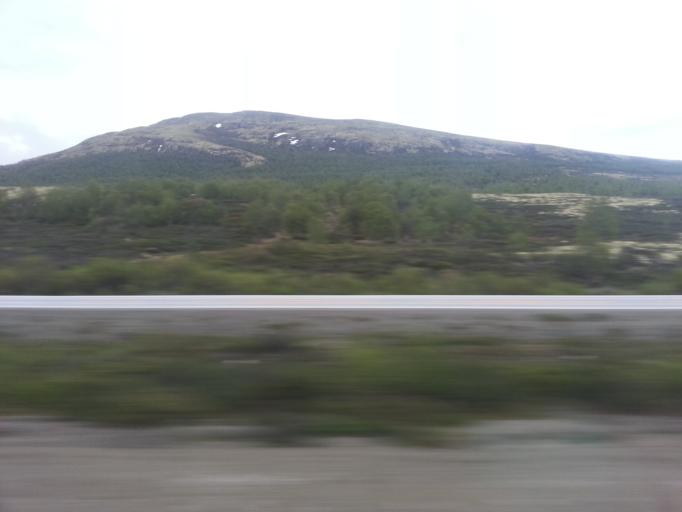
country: NO
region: Sor-Trondelag
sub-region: Oppdal
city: Oppdal
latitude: 62.2545
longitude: 9.5443
